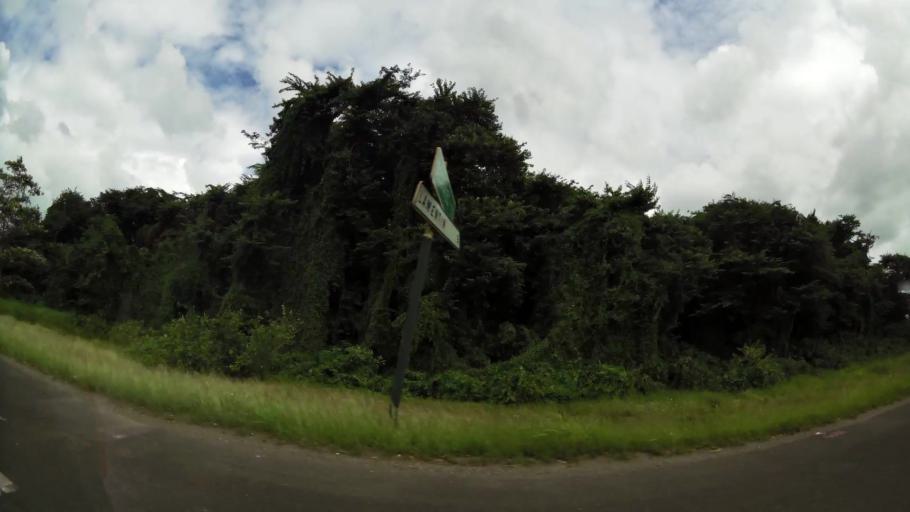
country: GP
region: Guadeloupe
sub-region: Guadeloupe
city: Baie-Mahault
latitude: 16.2567
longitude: -61.6023
